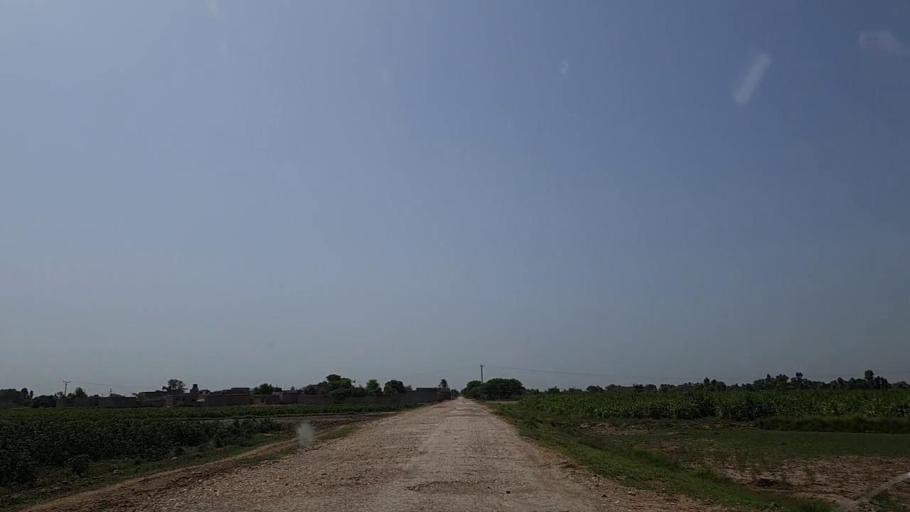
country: PK
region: Sindh
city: Naushahro Firoz
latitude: 26.8514
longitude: 68.0097
